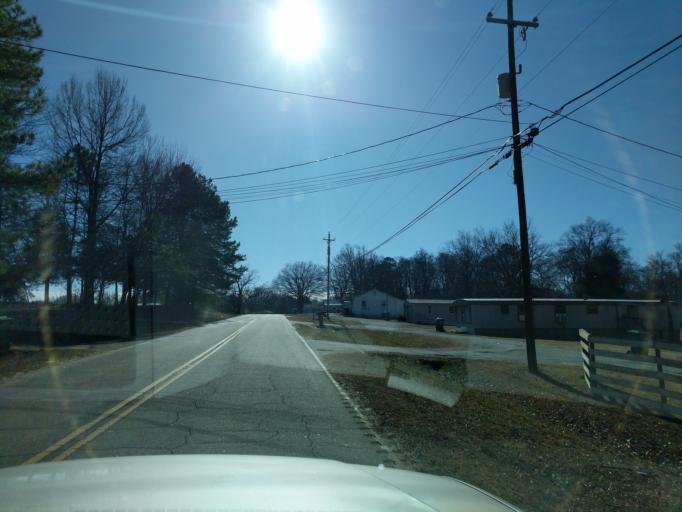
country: US
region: South Carolina
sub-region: Laurens County
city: Clinton
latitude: 34.4886
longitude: -81.8831
